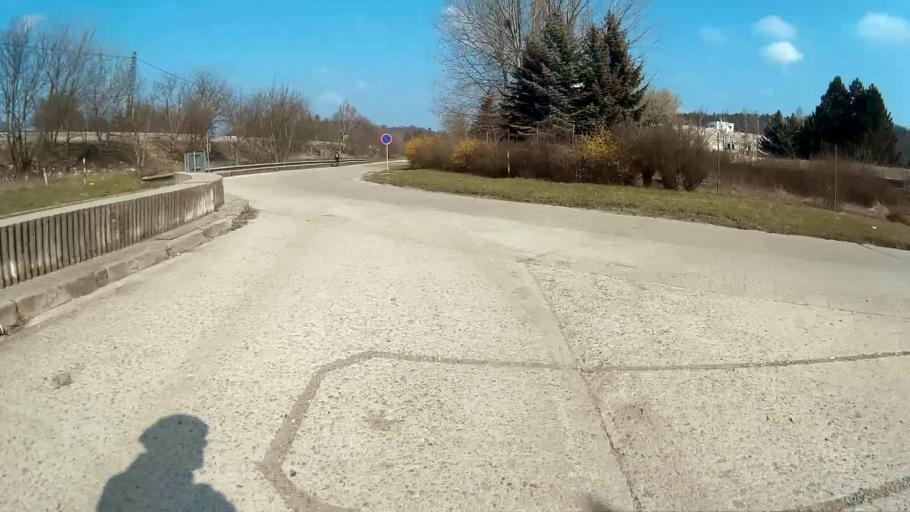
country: CZ
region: South Moravian
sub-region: Mesto Brno
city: Mokra Hora
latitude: 49.2518
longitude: 16.5912
